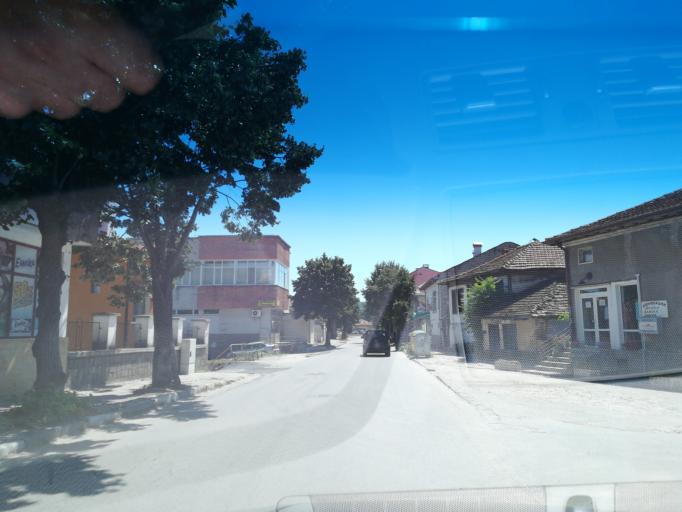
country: BG
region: Pazardzhik
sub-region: Obshtina Strelcha
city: Strelcha
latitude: 42.5051
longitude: 24.3210
